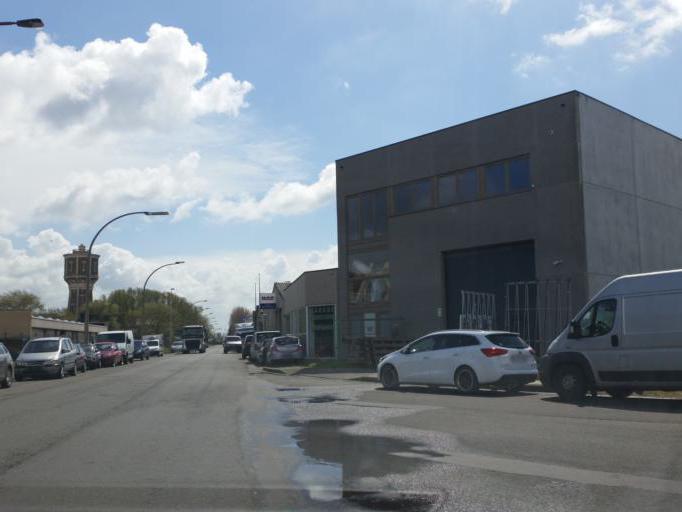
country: BE
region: Flanders
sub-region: Provincie West-Vlaanderen
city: Ostend
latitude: 51.2342
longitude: 2.9391
